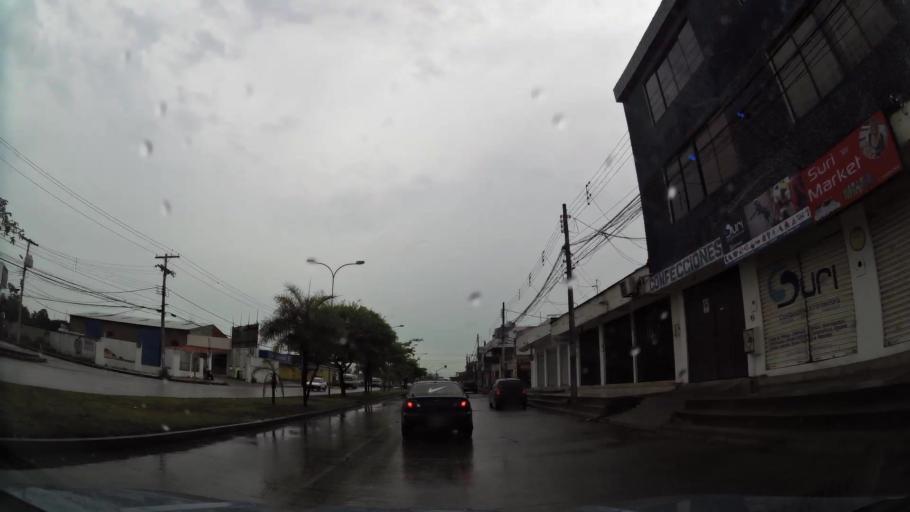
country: BO
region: Santa Cruz
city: Santa Cruz de la Sierra
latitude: -17.7690
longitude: -63.1543
